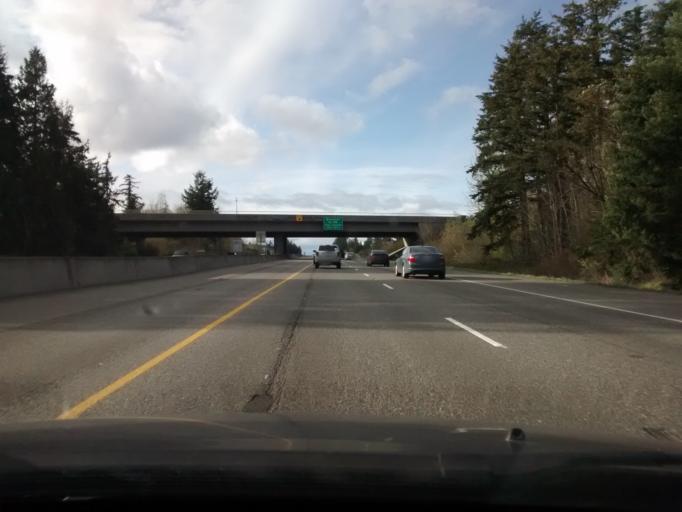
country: US
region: Washington
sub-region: Pierce County
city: Gig Harbor
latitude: 47.3042
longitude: -122.5754
